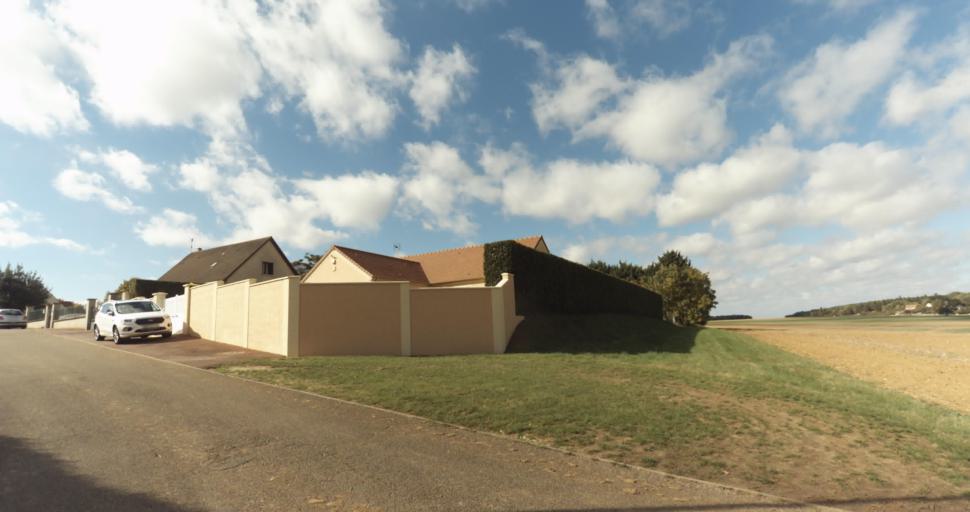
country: FR
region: Centre
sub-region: Departement d'Eure-et-Loir
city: Garnay
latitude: 48.7180
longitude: 1.3370
